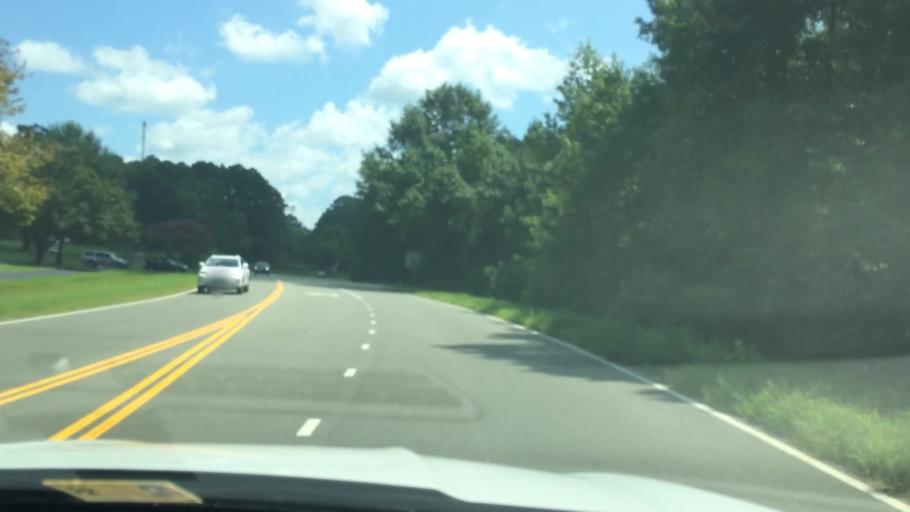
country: US
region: Virginia
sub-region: James City County
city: Williamsburg
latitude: 37.2959
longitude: -76.7386
